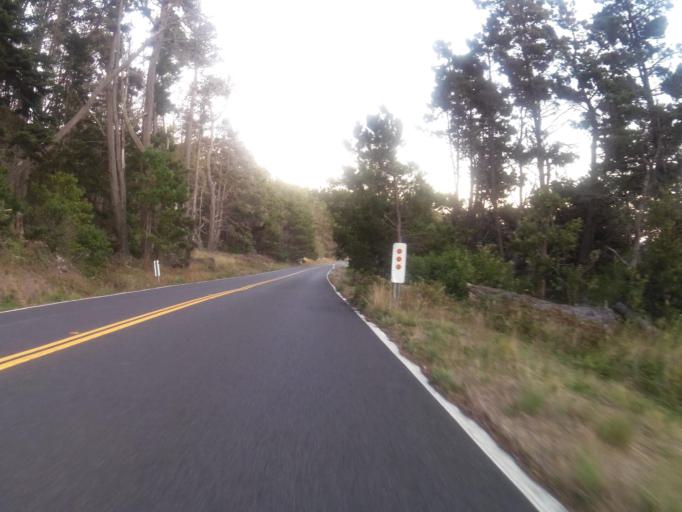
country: US
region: California
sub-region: Sonoma County
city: Sea Ranch
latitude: 38.6027
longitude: -123.3545
